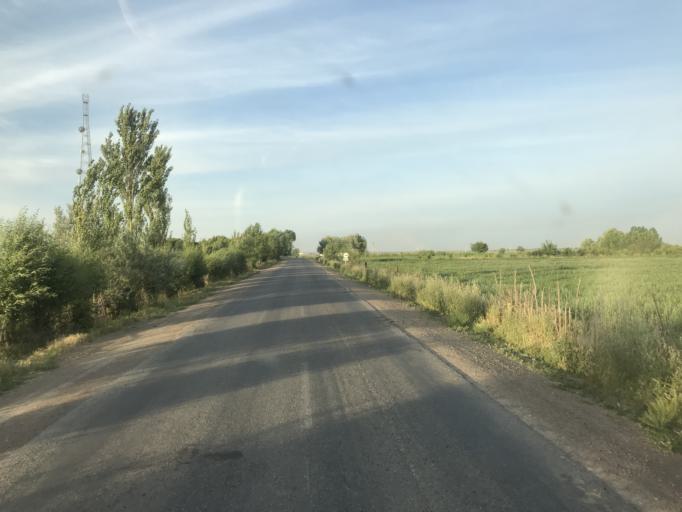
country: KZ
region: Ongtustik Qazaqstan
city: Asykata
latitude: 40.9527
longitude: 68.4585
